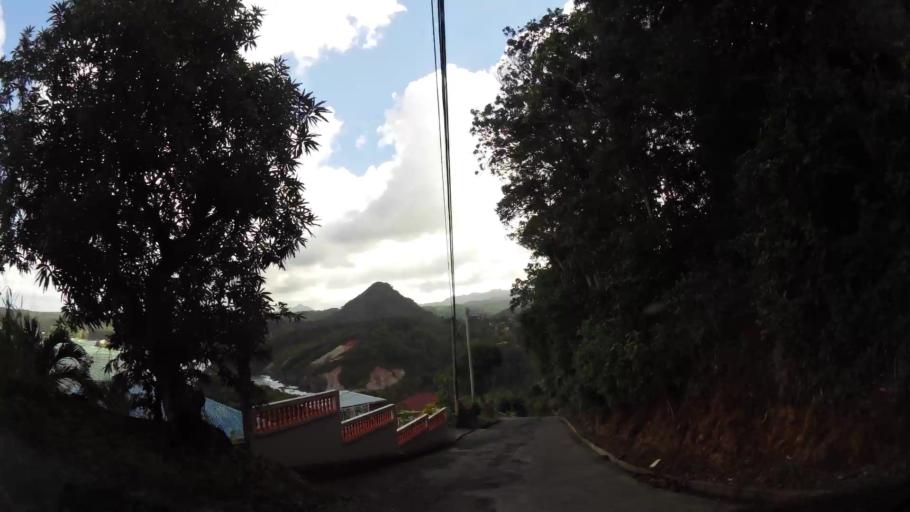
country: DM
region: Saint Andrew
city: Calibishie
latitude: 15.6036
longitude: -61.3961
